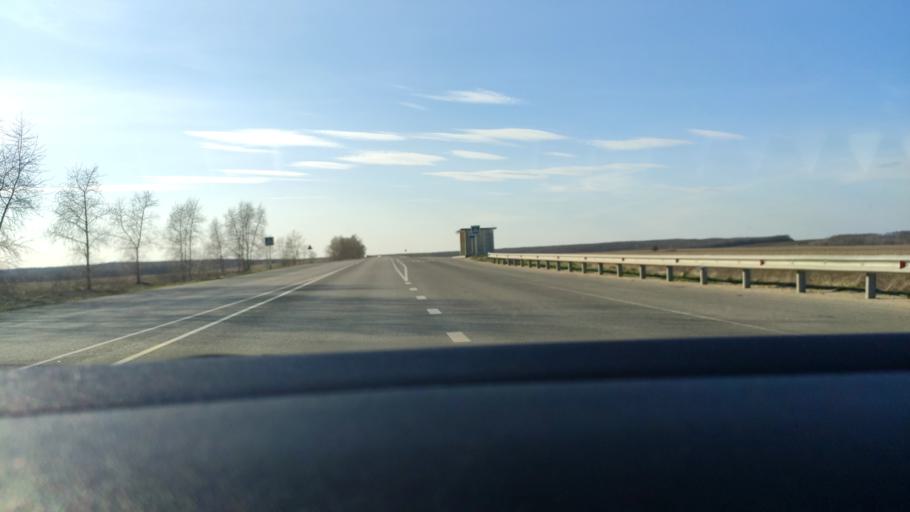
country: RU
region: Voronezj
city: Kolodeznyy
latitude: 51.3329
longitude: 39.0905
